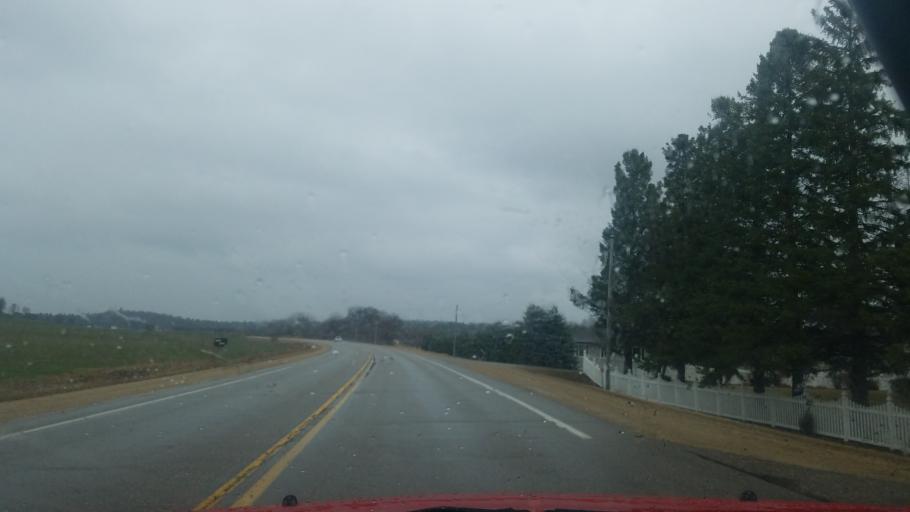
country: US
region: Wisconsin
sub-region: Dunn County
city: Tainter Lake
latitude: 44.9574
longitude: -91.8976
